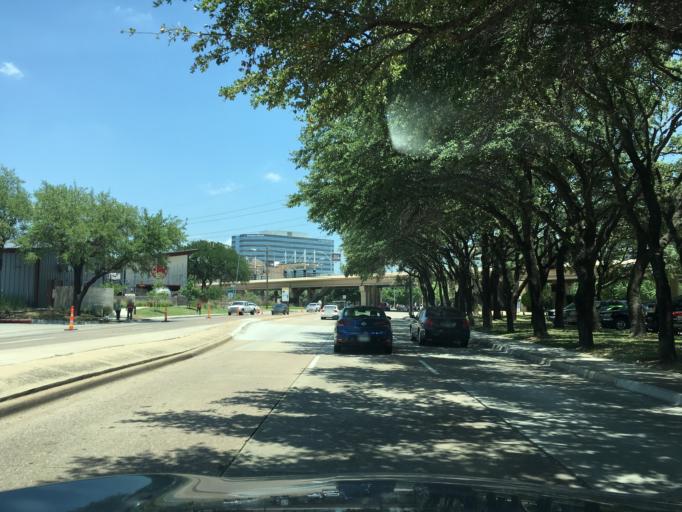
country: US
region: Texas
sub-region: Dallas County
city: University Park
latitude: 32.8817
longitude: -96.7659
